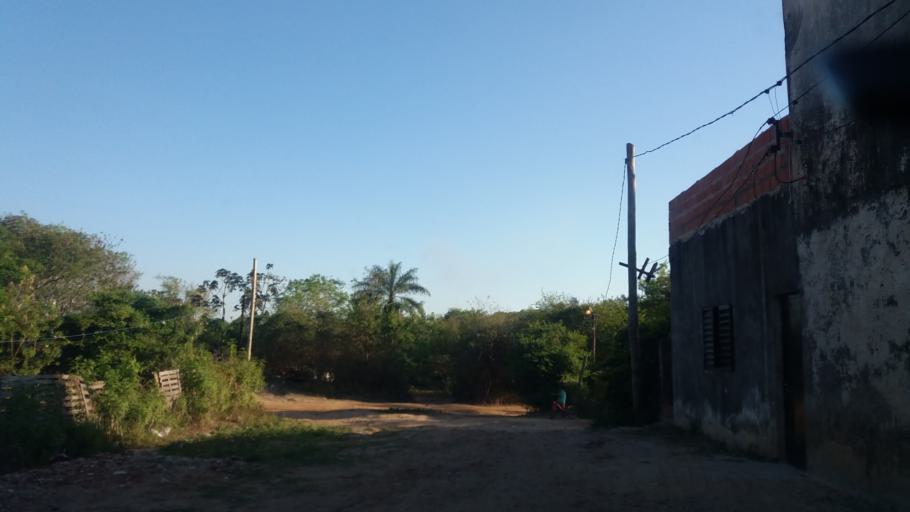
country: AR
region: Corrientes
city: Corrientes
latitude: -27.5161
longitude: -58.8320
